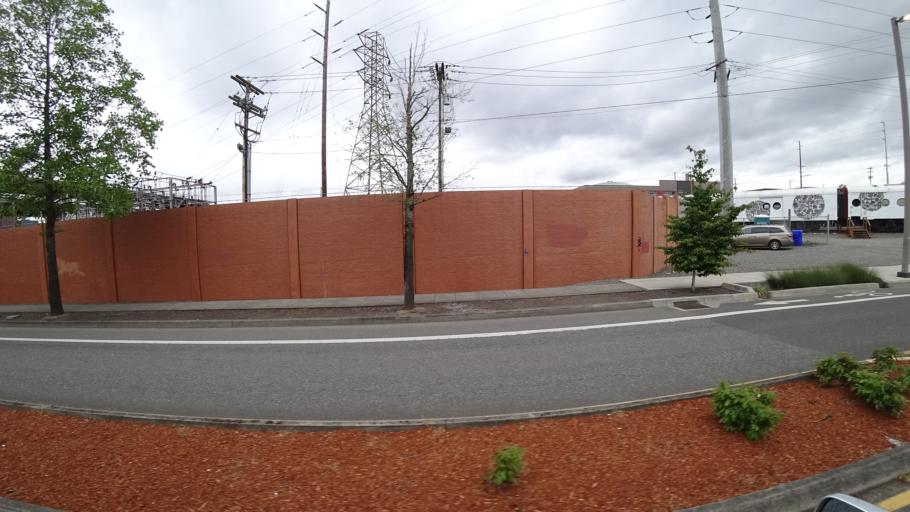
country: US
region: Oregon
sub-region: Multnomah County
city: Portland
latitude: 45.5085
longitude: -122.6645
